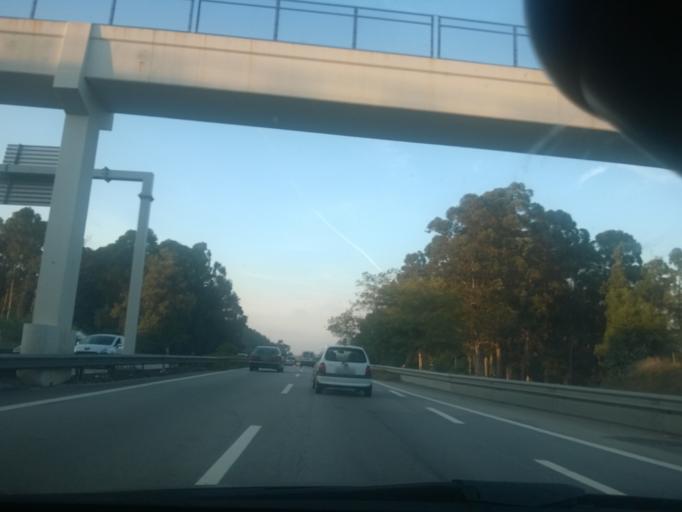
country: PT
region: Porto
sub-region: Maia
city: Leca do Bailio
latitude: 41.2075
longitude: -8.6272
